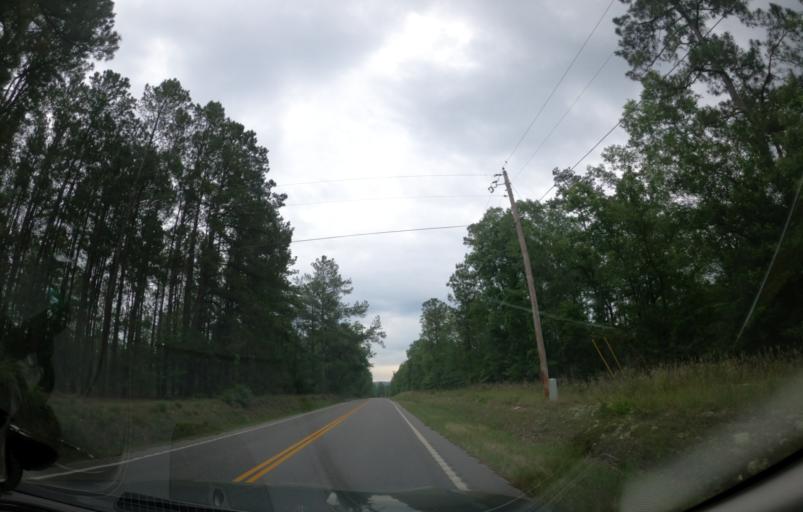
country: US
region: South Carolina
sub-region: Aiken County
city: Aiken
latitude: 33.5748
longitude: -81.6352
